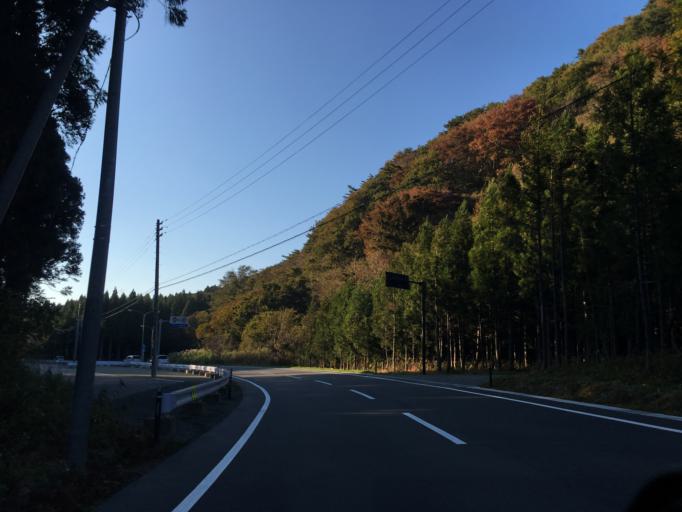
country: JP
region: Fukushima
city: Inawashiro
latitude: 37.3978
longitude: 140.1601
